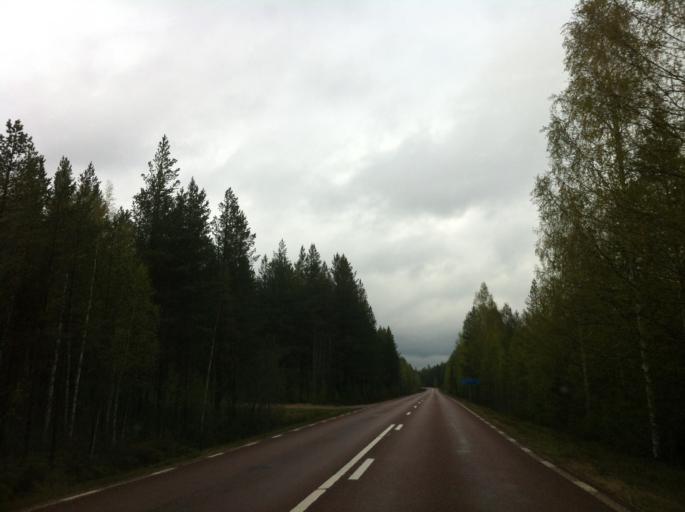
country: SE
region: Jaemtland
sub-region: Harjedalens Kommun
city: Sveg
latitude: 61.8812
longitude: 14.6278
